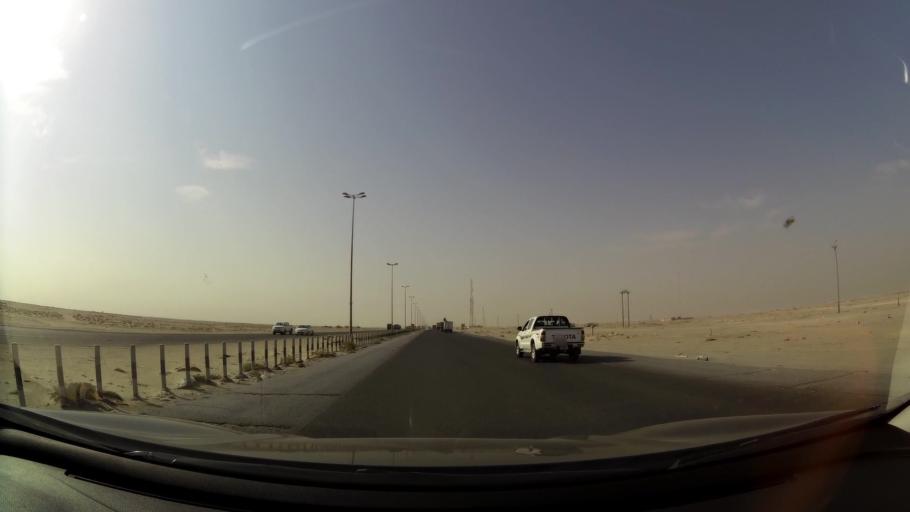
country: KW
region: Al Ahmadi
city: Al Ahmadi
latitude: 28.9104
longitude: 48.0961
